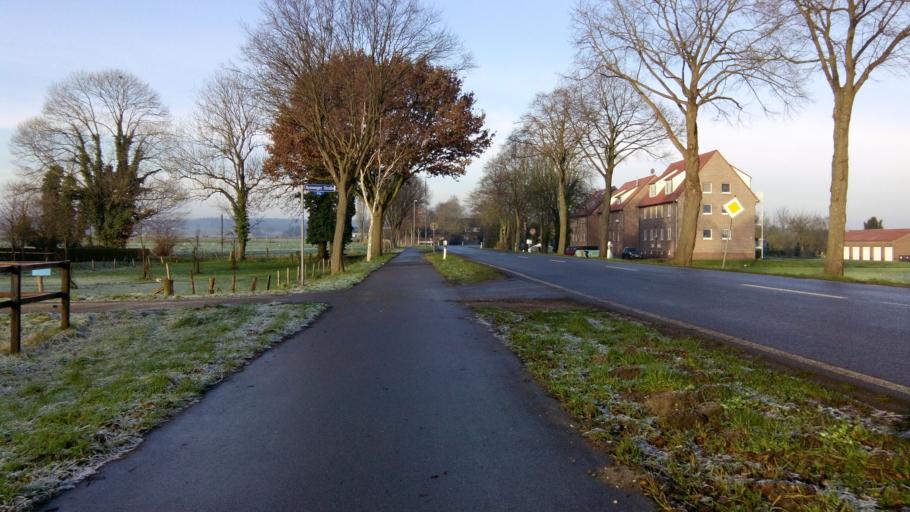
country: NL
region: Gelderland
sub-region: Gemeente Groesbeek
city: De Horst
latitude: 51.7966
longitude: 5.9830
